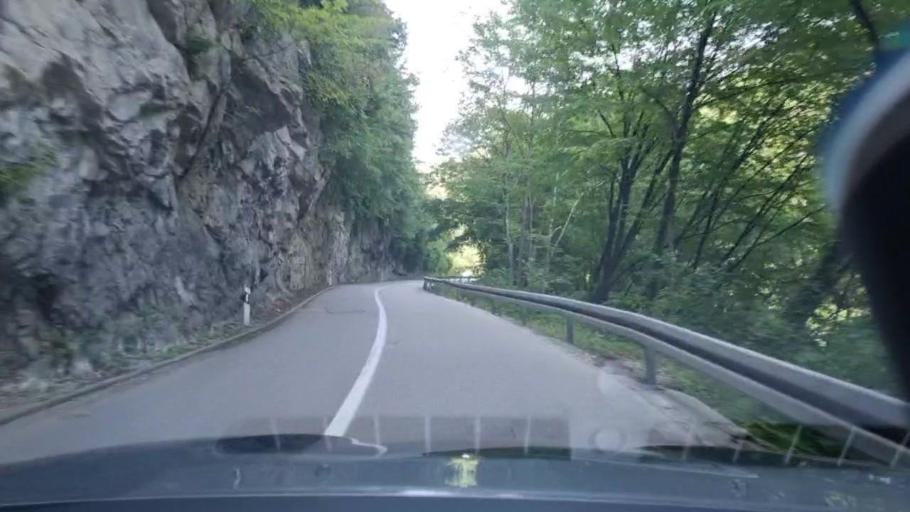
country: BA
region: Federation of Bosnia and Herzegovina
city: Stijena
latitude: 44.8931
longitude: 16.0481
